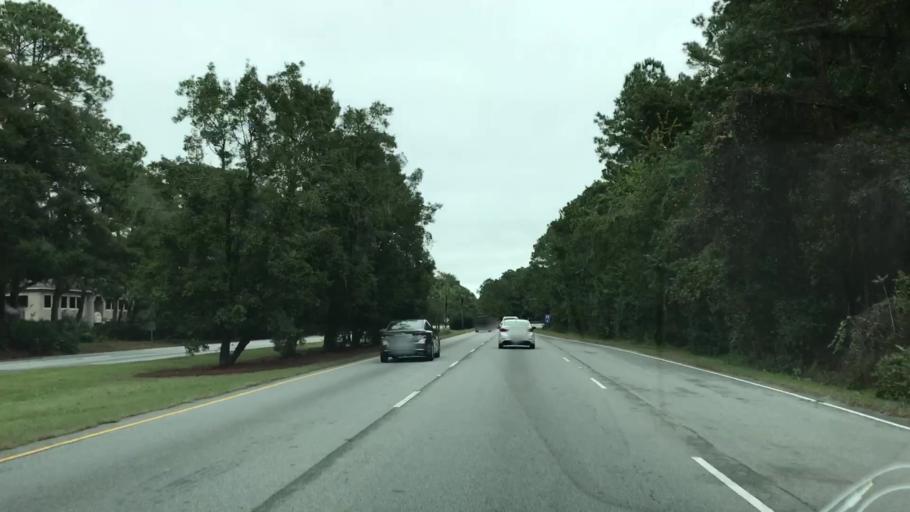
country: US
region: South Carolina
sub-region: Beaufort County
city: Hilton Head Island
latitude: 32.2156
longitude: -80.7193
